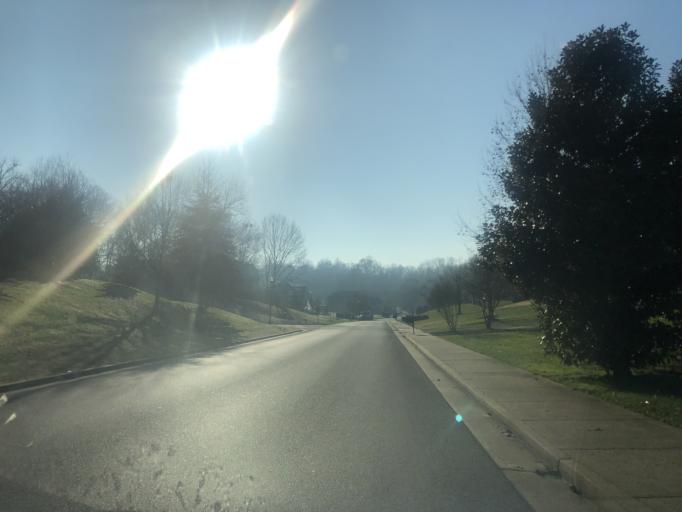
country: US
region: Tennessee
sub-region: Williamson County
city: Brentwood Estates
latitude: 35.9955
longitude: -86.7247
